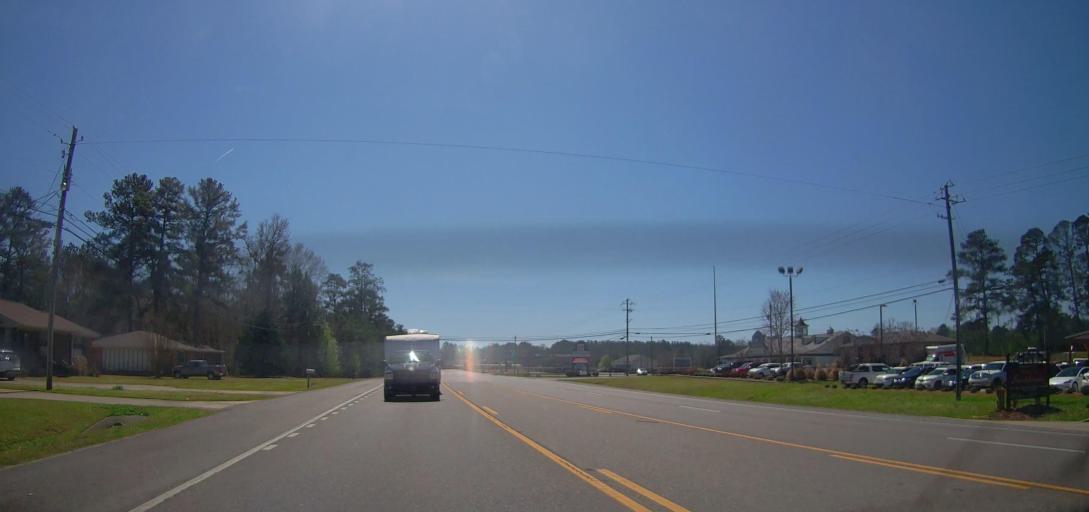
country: US
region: Alabama
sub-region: Etowah County
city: Southside
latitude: 33.9362
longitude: -86.0240
